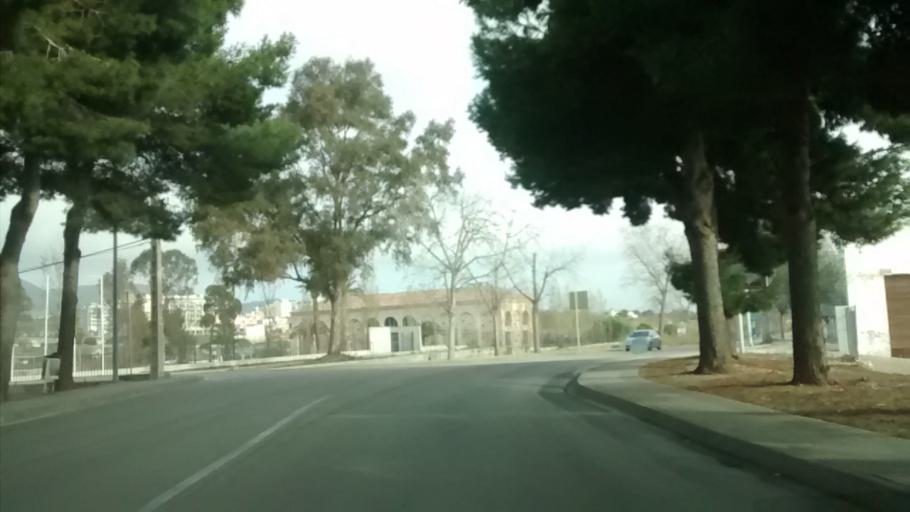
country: ES
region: Catalonia
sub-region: Provincia de Tarragona
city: Sant Carles de la Rapita
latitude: 40.6205
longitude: 0.5989
